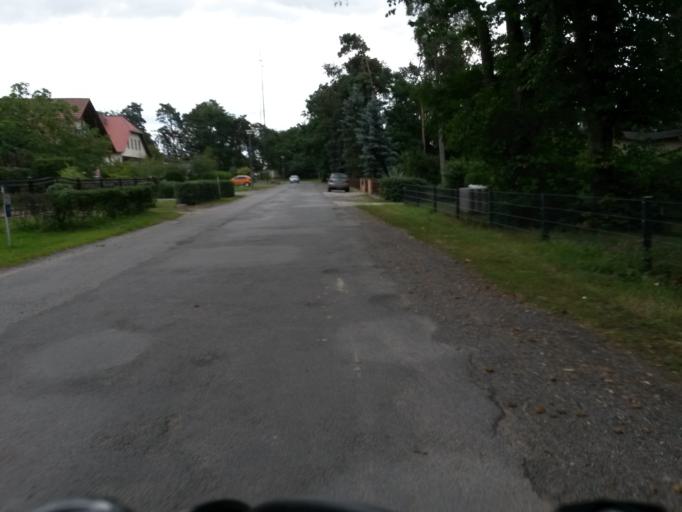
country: DE
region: Brandenburg
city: Angermunde
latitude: 53.0031
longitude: 13.9832
